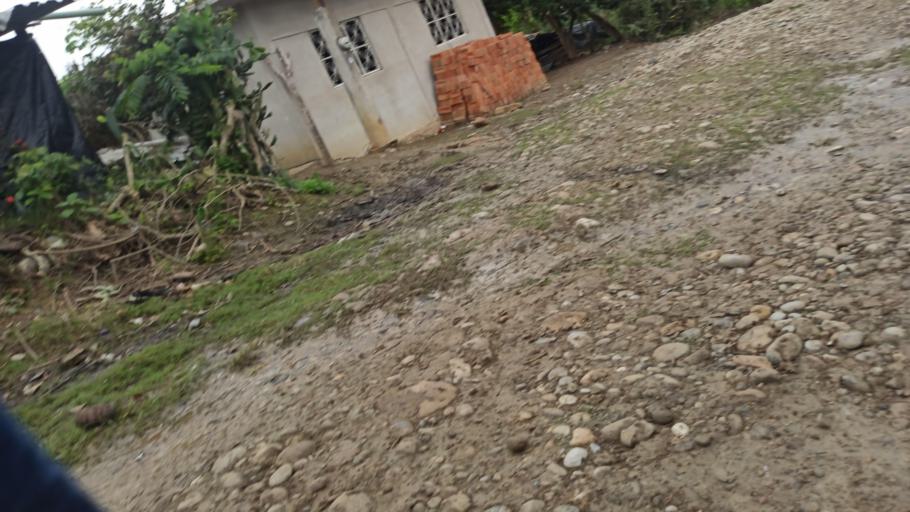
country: MX
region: Veracruz
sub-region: Papantla
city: El Chote
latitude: 20.3831
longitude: -97.3562
